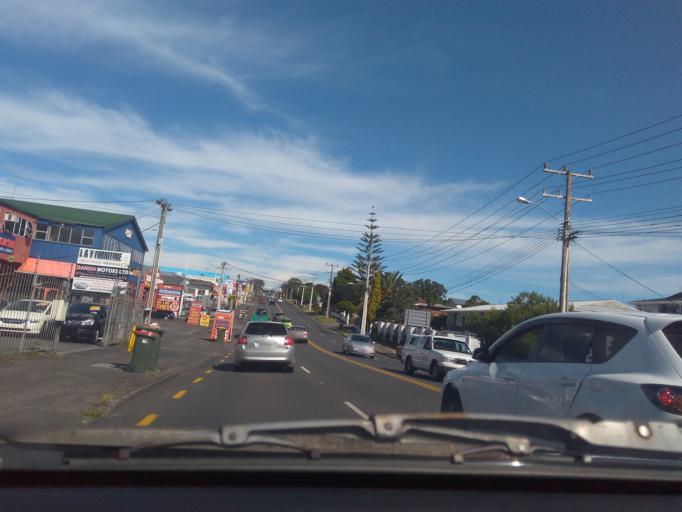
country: NZ
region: Auckland
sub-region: Auckland
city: Waitakere
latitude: -36.9026
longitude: 174.6563
